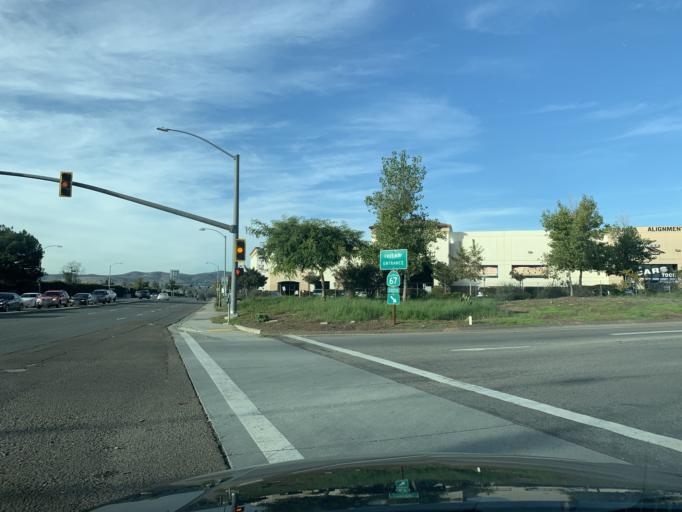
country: US
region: California
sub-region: San Diego County
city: Santee
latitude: 32.8330
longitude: -116.9642
